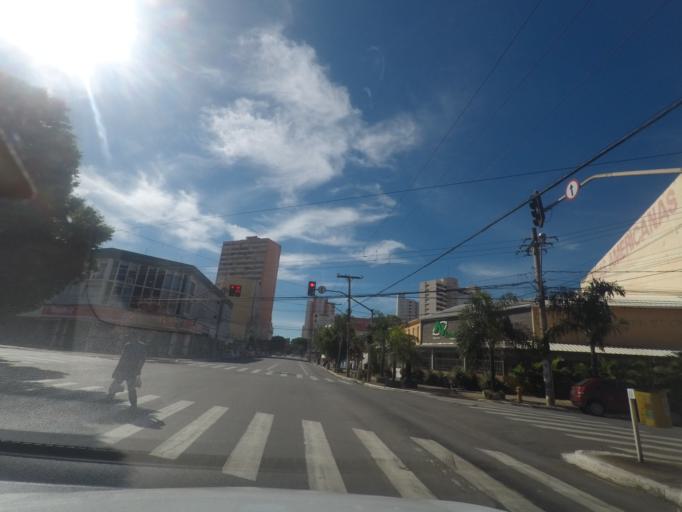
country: BR
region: Goias
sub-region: Goiania
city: Goiania
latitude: -16.6749
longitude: -49.2626
